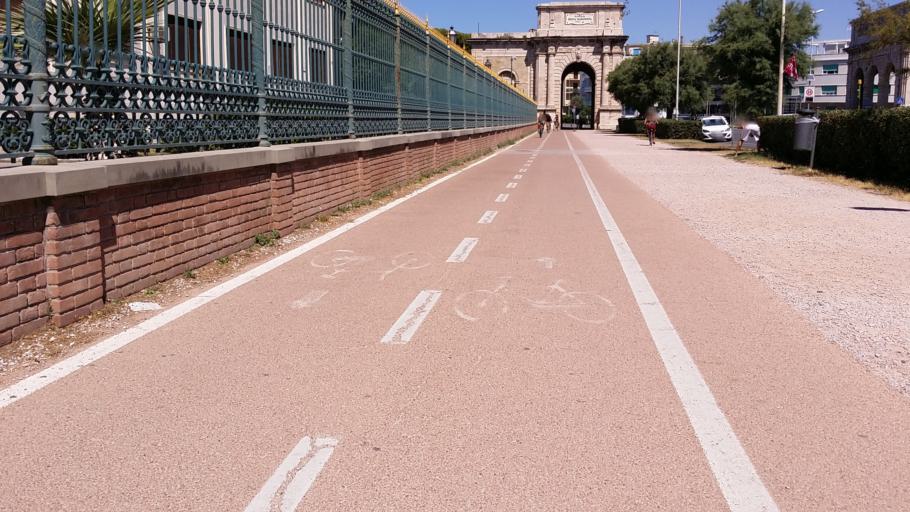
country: IT
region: Tuscany
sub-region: Provincia di Livorno
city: Livorno
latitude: 43.5270
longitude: 10.3103
